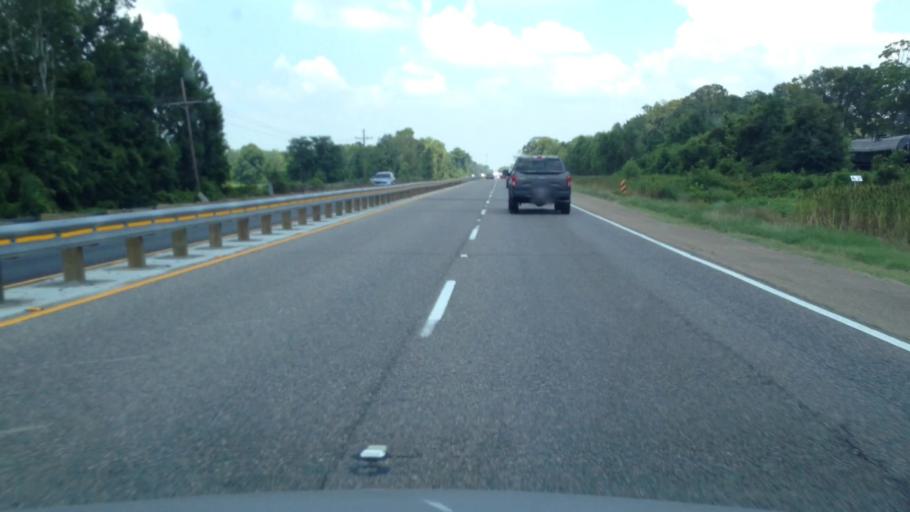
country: US
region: Louisiana
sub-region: Pointe Coupee Parish
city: Livonia
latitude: 30.5560
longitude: -91.6130
